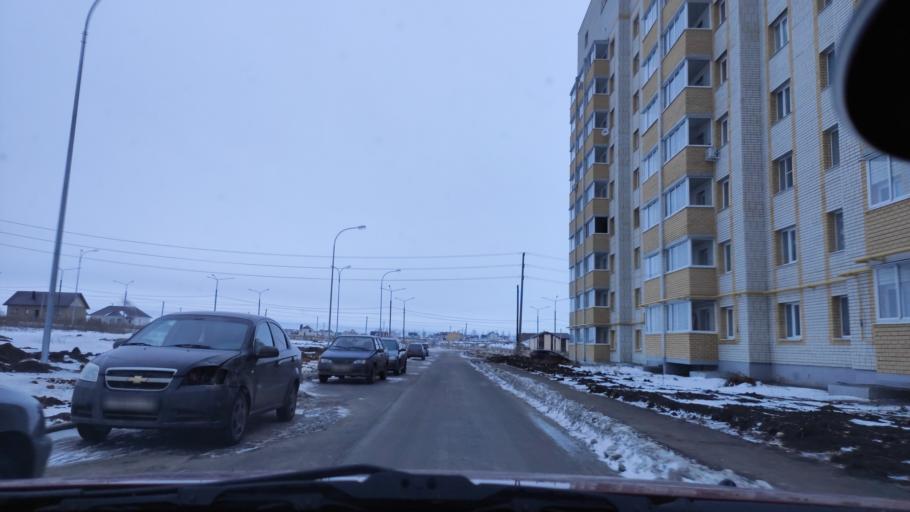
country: RU
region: Tambov
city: Tambov
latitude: 52.7832
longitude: 41.4188
